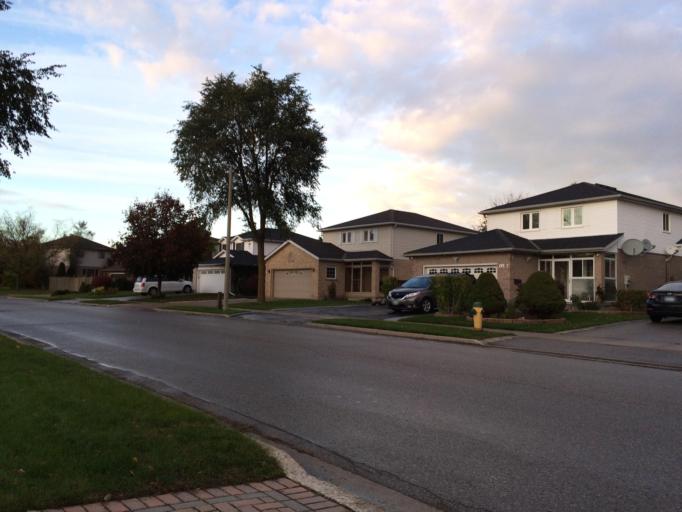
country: CA
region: Ontario
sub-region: Wellington County
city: Guelph
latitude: 43.5280
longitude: -80.2971
